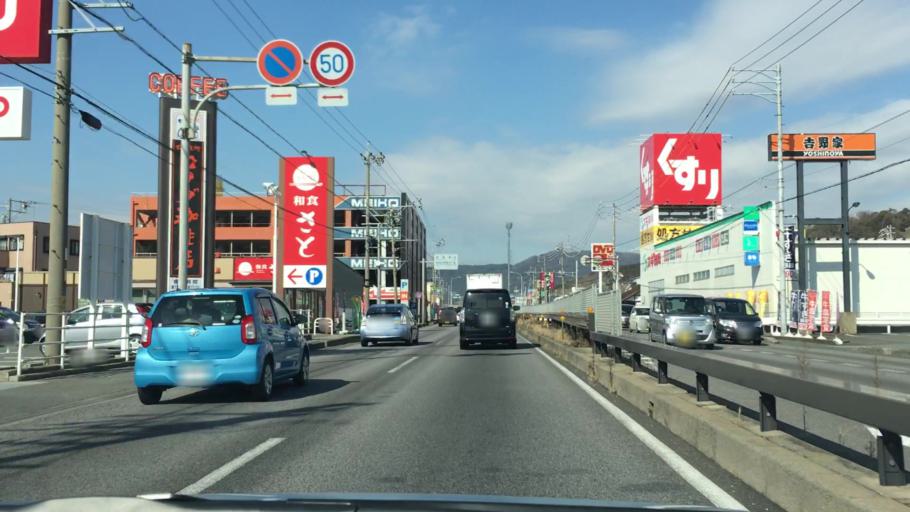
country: JP
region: Aichi
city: Kozakai-cho
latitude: 34.8434
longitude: 137.3229
